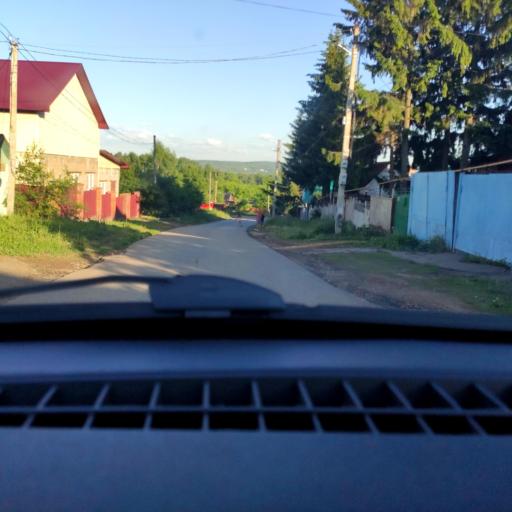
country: RU
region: Bashkortostan
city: Avdon
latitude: 54.6184
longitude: 55.6517
